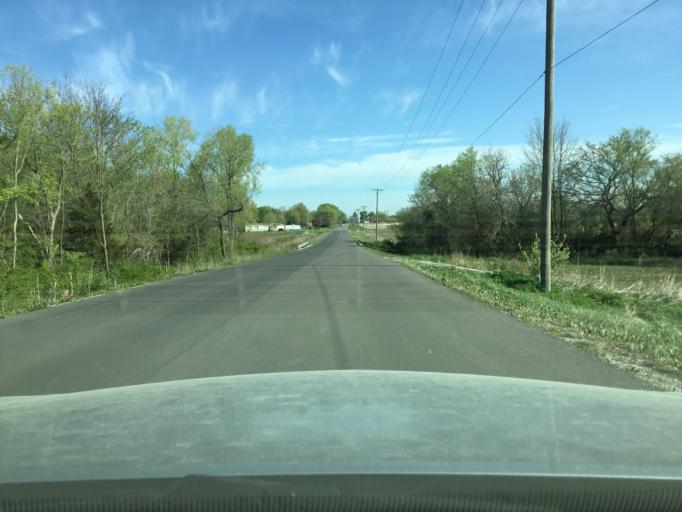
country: US
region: Kansas
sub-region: Neosho County
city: Chanute
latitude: 37.6577
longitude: -95.4435
